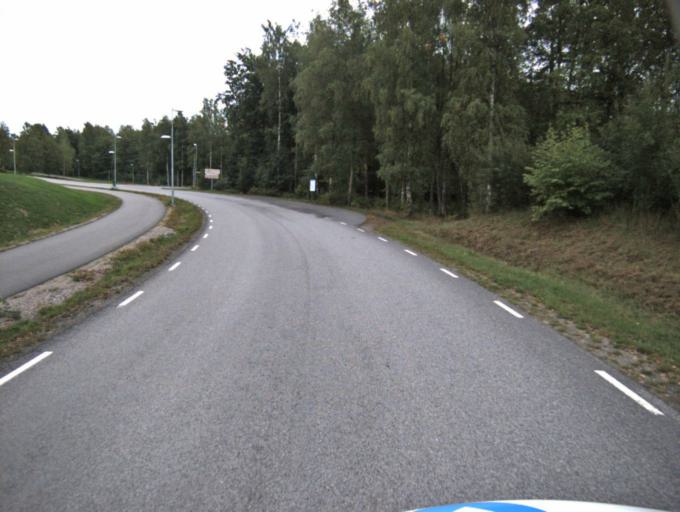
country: SE
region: Vaestra Goetaland
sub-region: Ulricehamns Kommun
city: Ulricehamn
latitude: 57.7855
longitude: 13.4321
